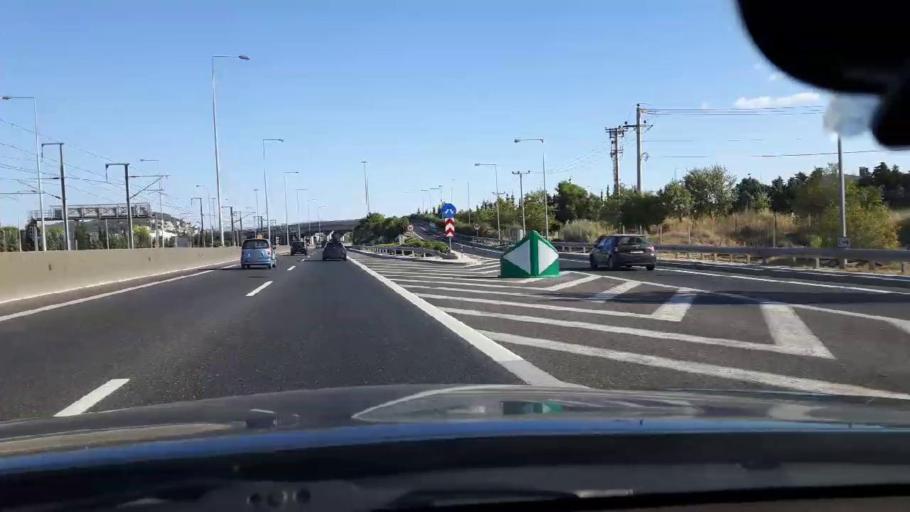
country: GR
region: Attica
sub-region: Nomarchia Anatolikis Attikis
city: Pallini
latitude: 37.9866
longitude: 23.8705
